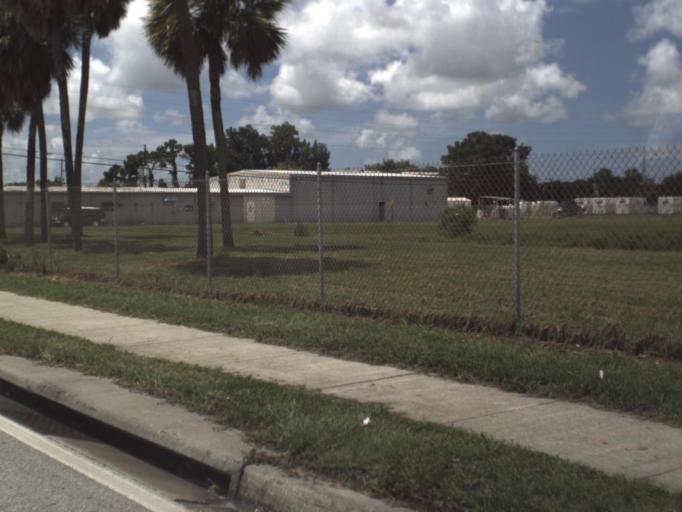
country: US
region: Florida
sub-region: Pinellas County
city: South Highpoint
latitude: 27.8980
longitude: -82.7006
